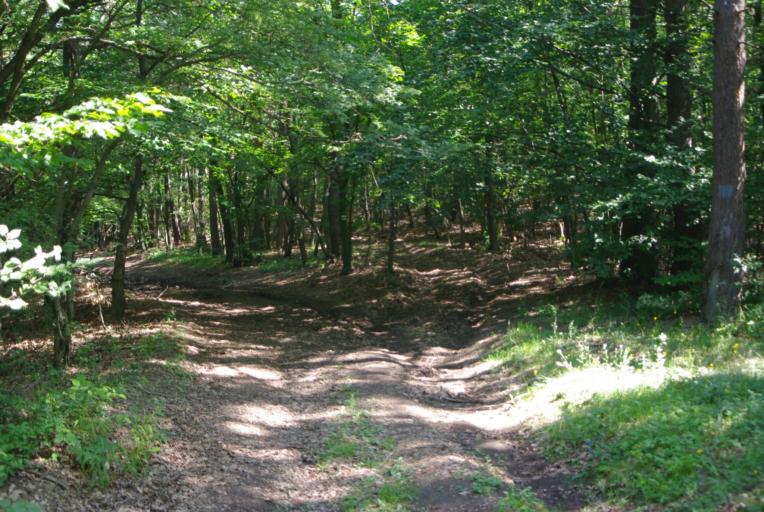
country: HU
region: Borsod-Abauj-Zemplen
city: Gonc
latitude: 48.4047
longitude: 21.3413
